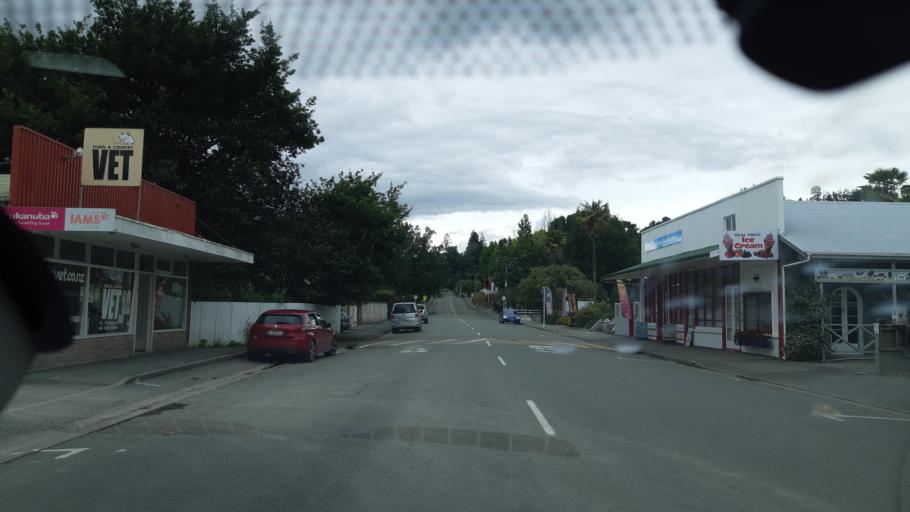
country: NZ
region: Tasman
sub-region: Tasman District
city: Wakefield
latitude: -41.4061
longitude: 173.0430
